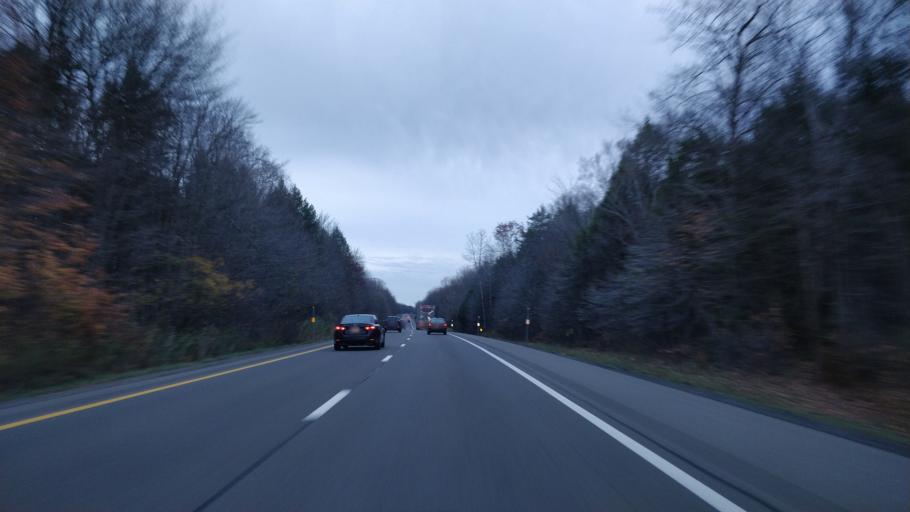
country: US
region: New York
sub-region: Oswego County
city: Central Square
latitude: 43.3875
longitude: -76.1187
